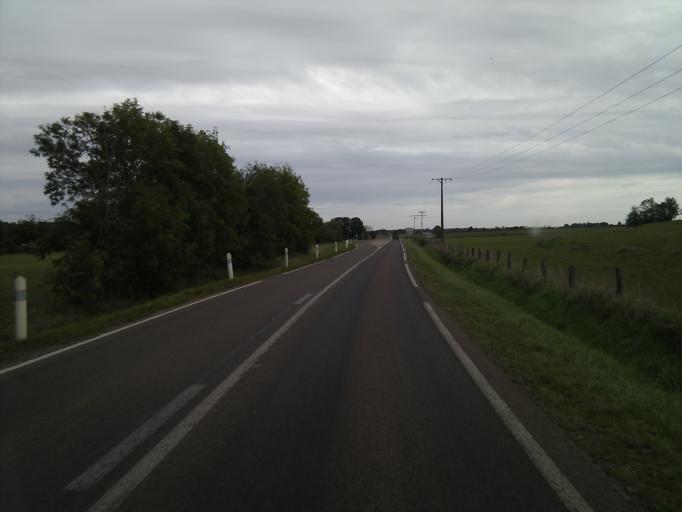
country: FR
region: Champagne-Ardenne
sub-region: Departement de la Haute-Marne
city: Chaumont
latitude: 48.0956
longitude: 5.0331
